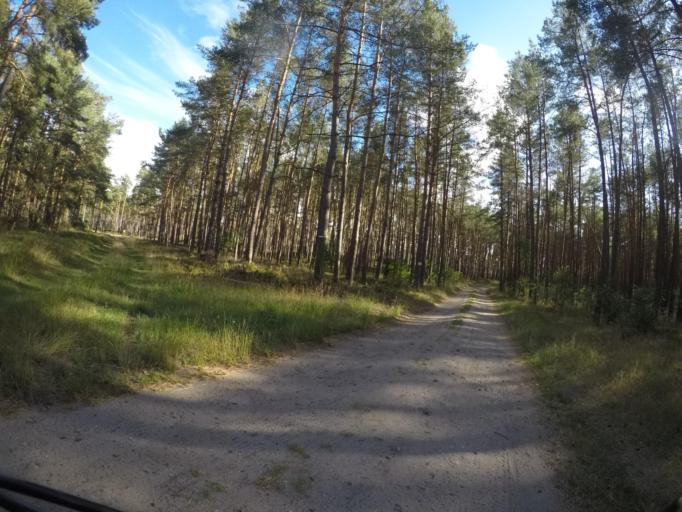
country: DE
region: Mecklenburg-Vorpommern
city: Lubtheen
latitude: 53.2588
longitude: 10.9930
